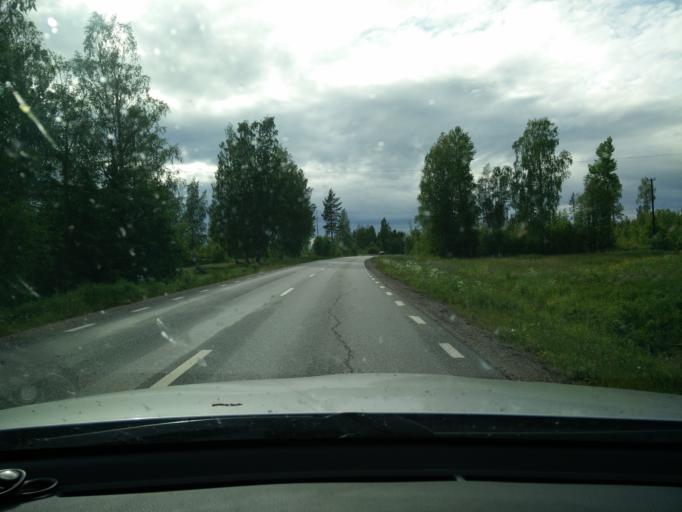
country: SE
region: Gaevleborg
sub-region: Nordanstigs Kommun
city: Bergsjoe
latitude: 62.0853
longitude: 16.7950
